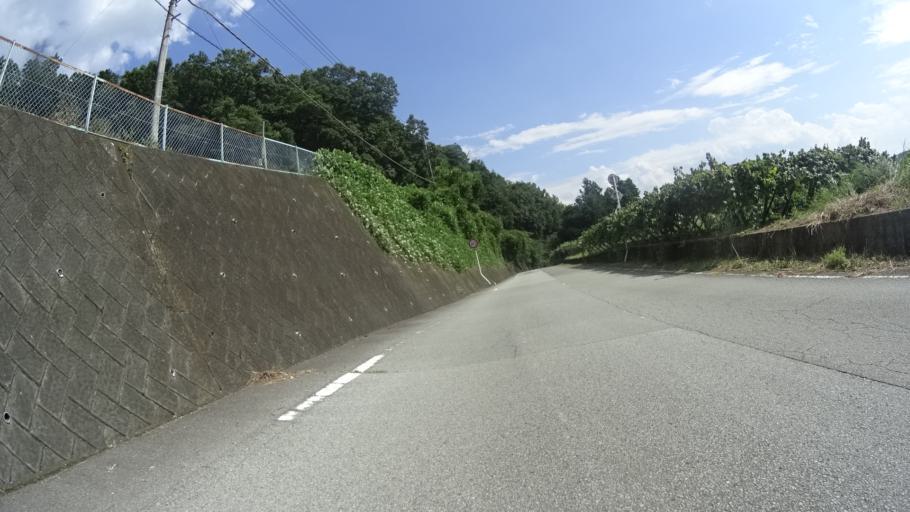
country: JP
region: Yamanashi
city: Enzan
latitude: 35.7567
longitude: 138.7101
